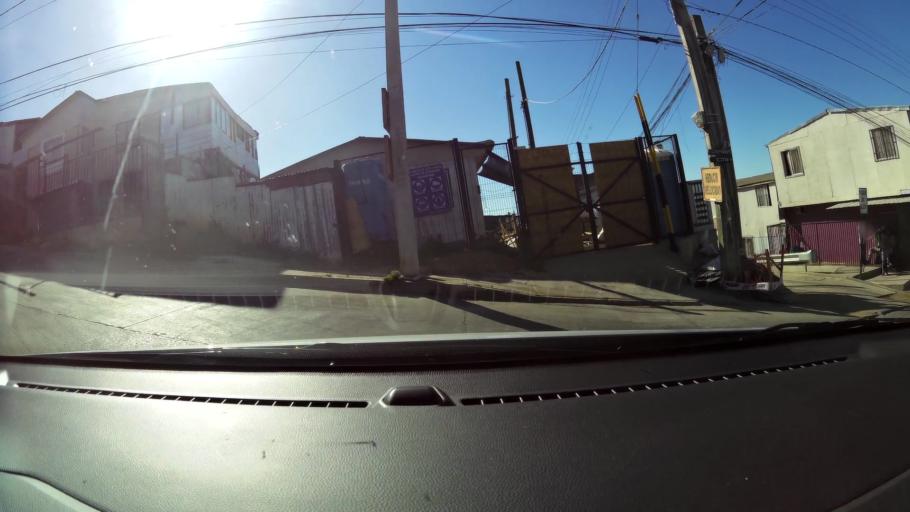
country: CL
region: Valparaiso
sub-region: Provincia de Valparaiso
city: Valparaiso
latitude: -33.0620
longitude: -71.6225
